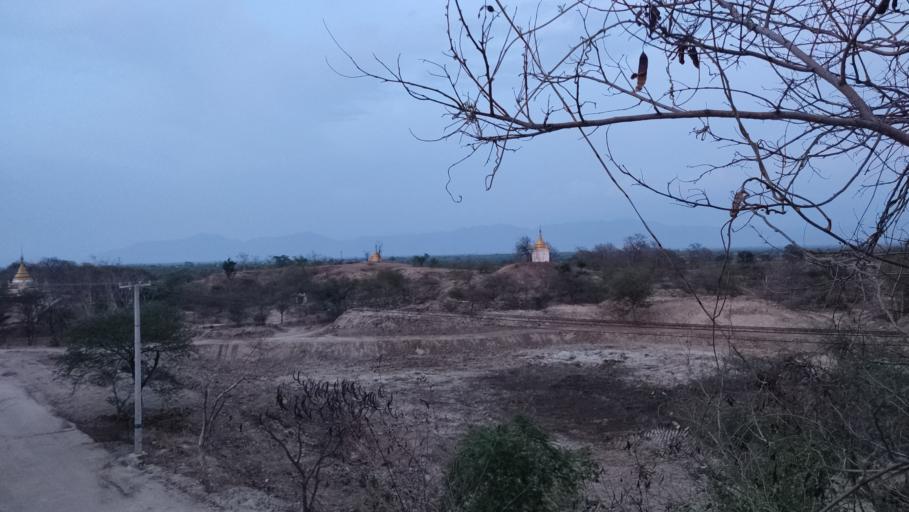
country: MM
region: Mandalay
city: Meiktila
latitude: 21.0837
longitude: 96.0176
